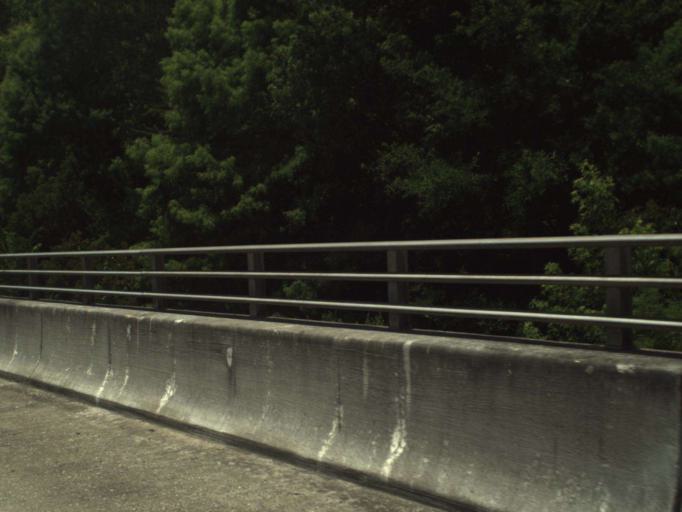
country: US
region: Florida
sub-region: Seminole County
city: Oviedo
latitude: 28.6900
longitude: -81.2503
